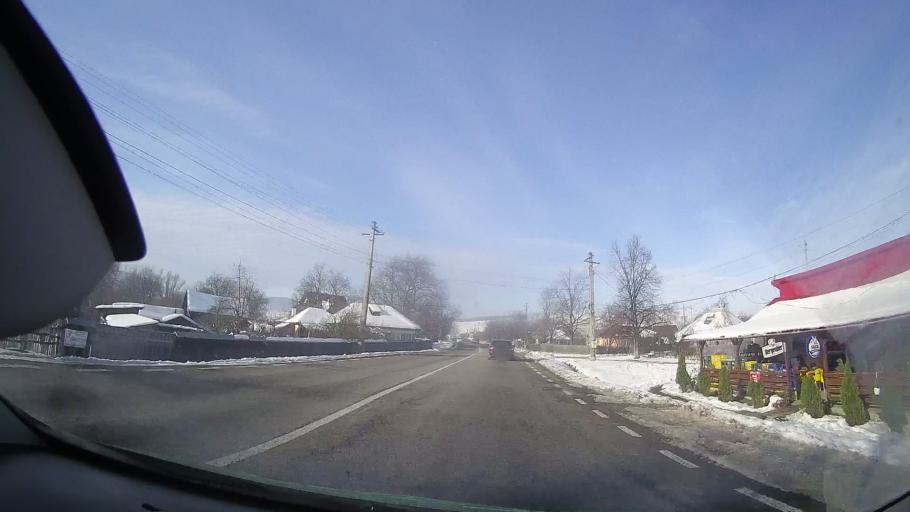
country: RO
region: Neamt
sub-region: Comuna Dobreni
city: Dobreni
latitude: 46.9953
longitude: 26.3918
